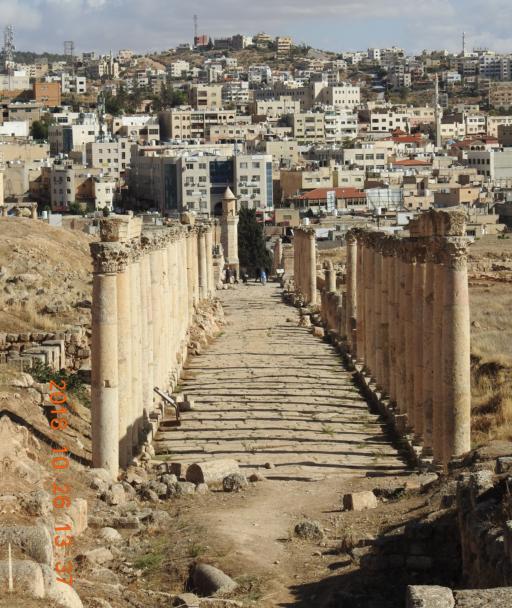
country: JO
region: Jerash
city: Jarash
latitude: 32.2800
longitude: 35.8898
